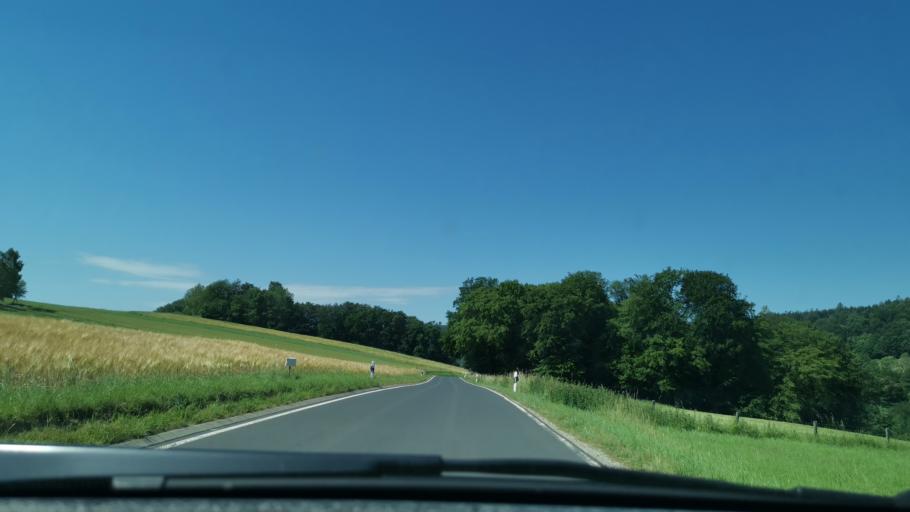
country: DE
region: Hesse
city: Hessisch Lichtenau
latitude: 51.1470
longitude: 9.7324
